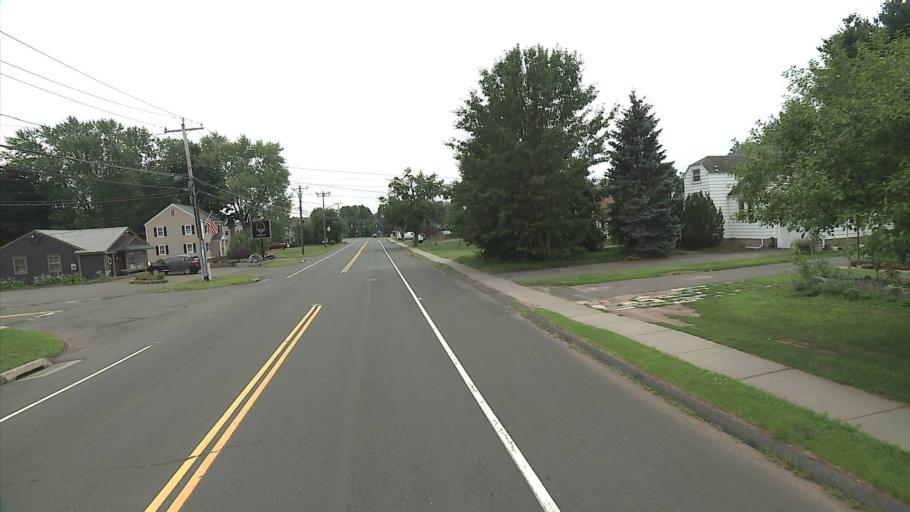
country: US
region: Connecticut
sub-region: Middlesex County
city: Cromwell
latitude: 41.6203
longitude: -72.6538
